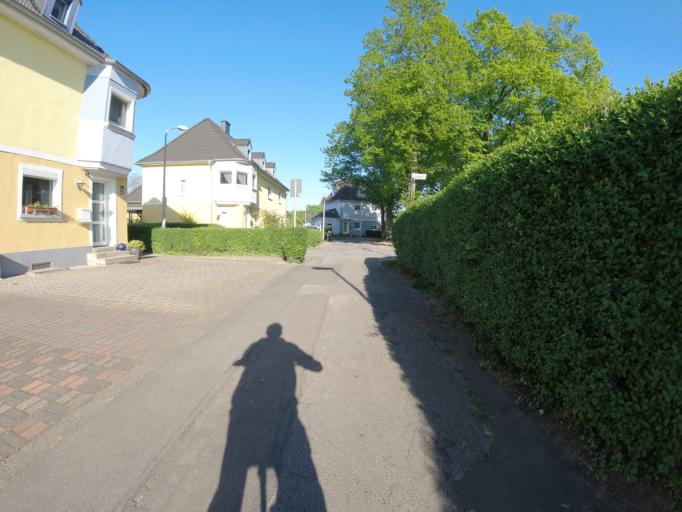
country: DE
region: North Rhine-Westphalia
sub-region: Regierungsbezirk Dusseldorf
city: Hochfeld
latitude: 51.3864
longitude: 6.7061
